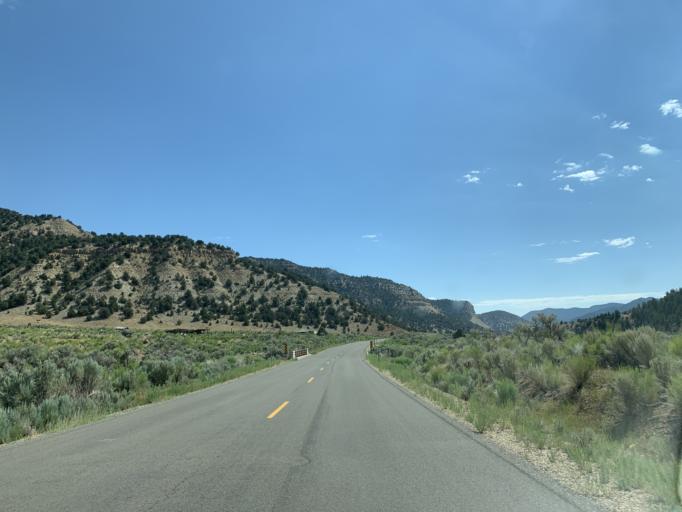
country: US
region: Utah
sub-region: Carbon County
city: East Carbon City
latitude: 39.7748
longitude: -110.5109
